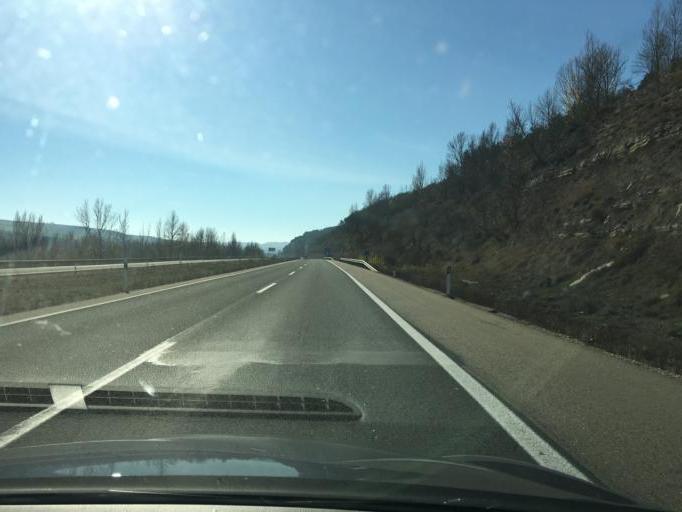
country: ES
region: Castille and Leon
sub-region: Provincia de Burgos
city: Pradanos de Bureba
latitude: 42.5212
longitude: -3.3397
